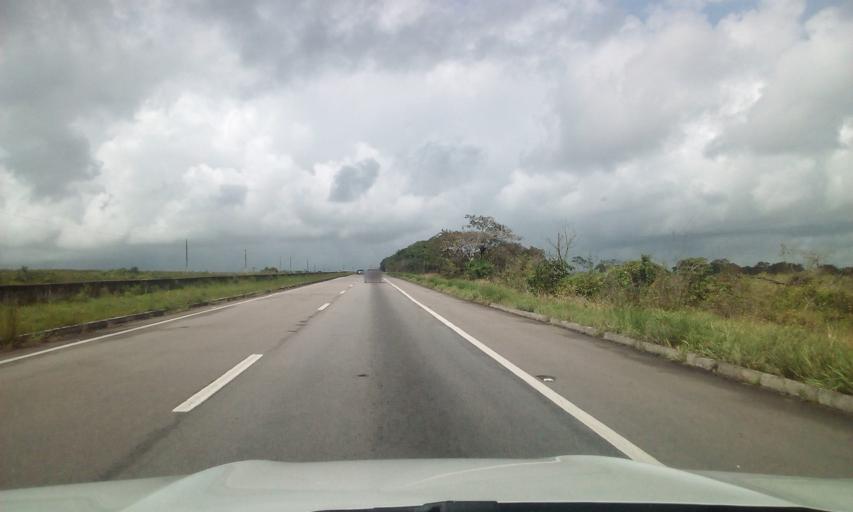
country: BR
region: Paraiba
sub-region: Alhandra
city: Alhandra
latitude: -7.4759
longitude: -34.9786
